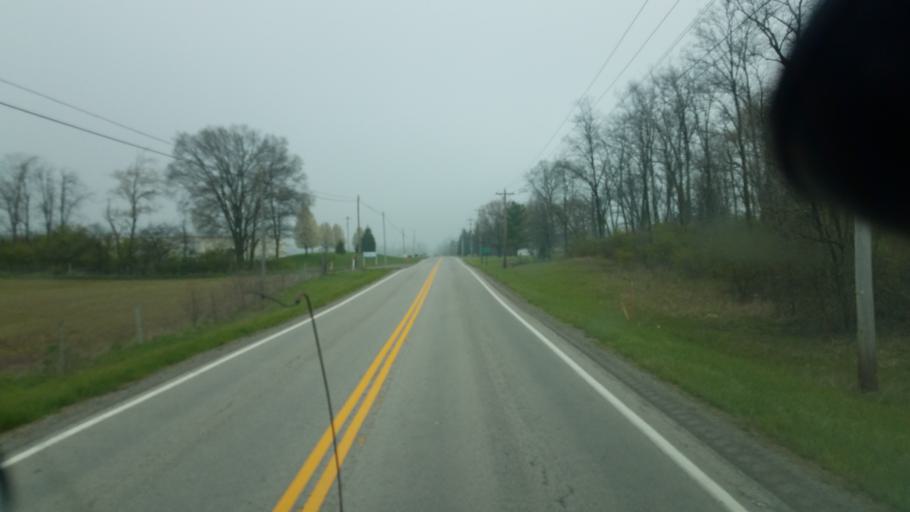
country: US
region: Ohio
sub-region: Logan County
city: Bellefontaine
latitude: 40.3688
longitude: -83.7915
